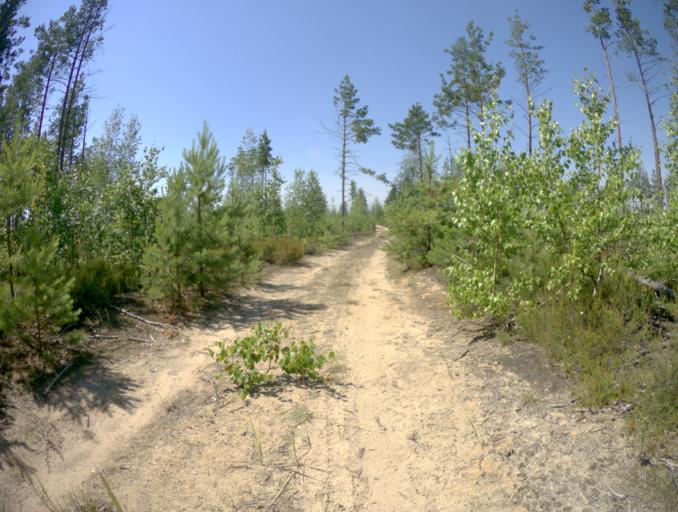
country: RU
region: Ivanovo
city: Talitsy
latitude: 56.4379
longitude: 42.2536
